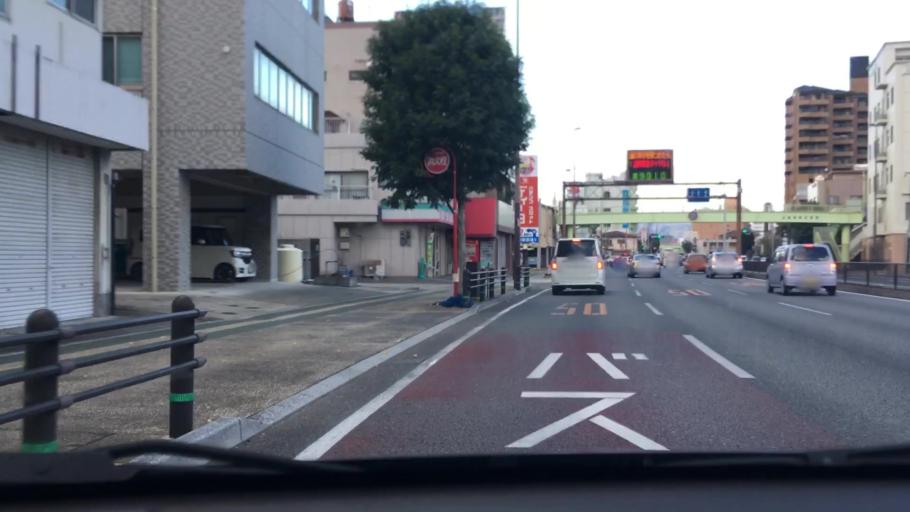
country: JP
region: Oita
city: Beppu
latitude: 33.2686
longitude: 131.5105
